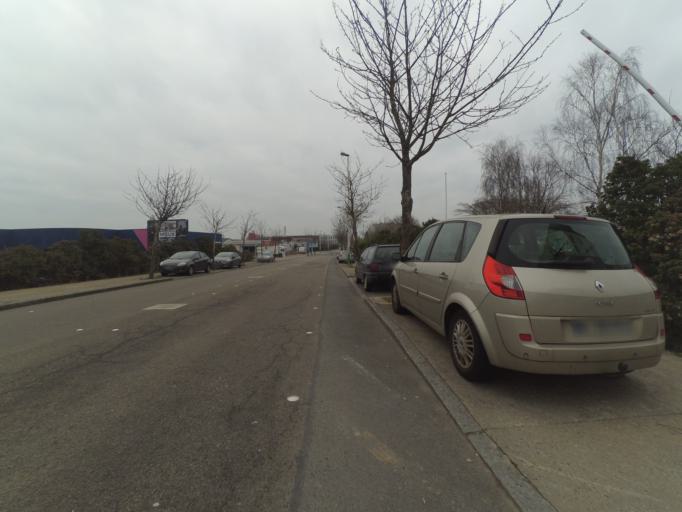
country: FR
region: Pays de la Loire
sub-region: Departement de la Loire-Atlantique
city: Saint-Herblain
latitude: 47.2203
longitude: -1.6403
